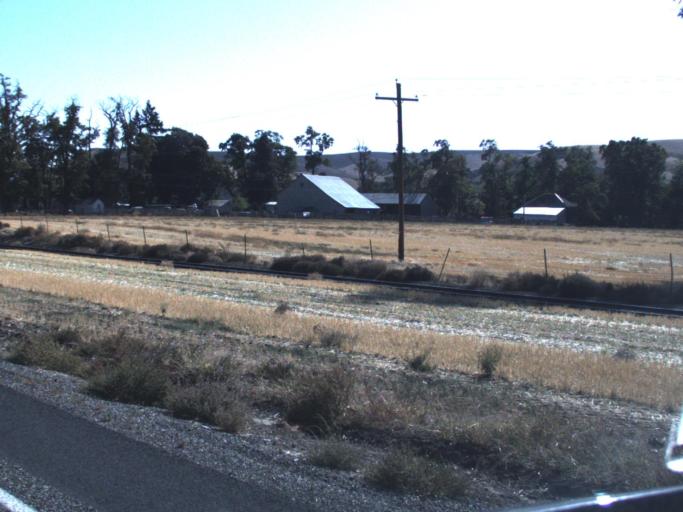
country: US
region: Washington
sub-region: Walla Walla County
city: Waitsburg
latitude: 46.2869
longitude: -118.2491
